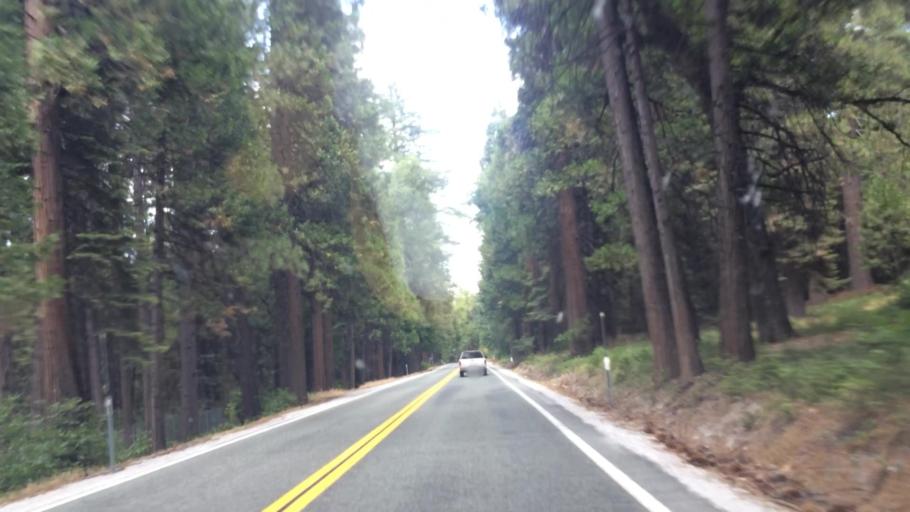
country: US
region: California
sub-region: Amador County
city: Pioneer
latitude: 38.5045
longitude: -120.4951
